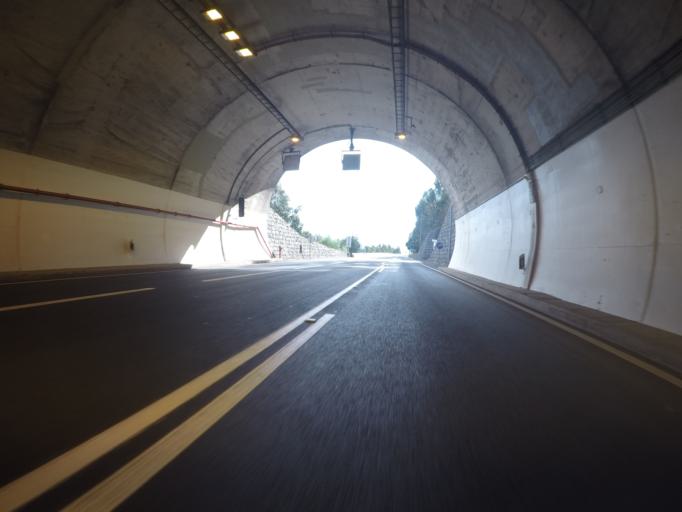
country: PT
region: Madeira
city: Canico
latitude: 32.6537
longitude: -16.8509
